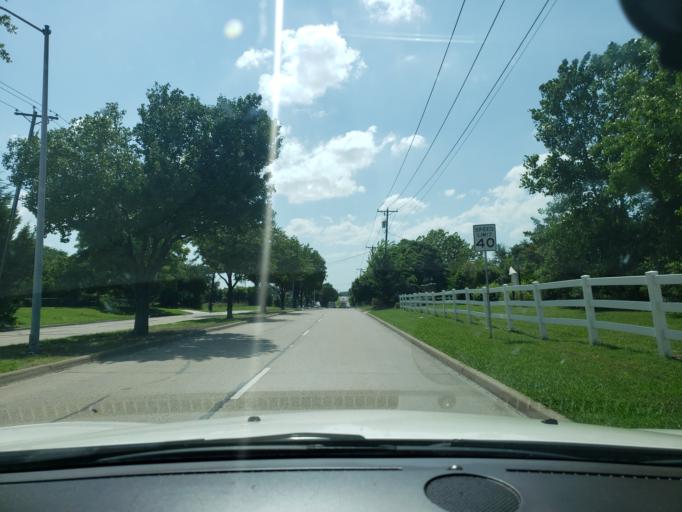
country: US
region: Texas
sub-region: Dallas County
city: Rowlett
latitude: 32.8938
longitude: -96.5657
